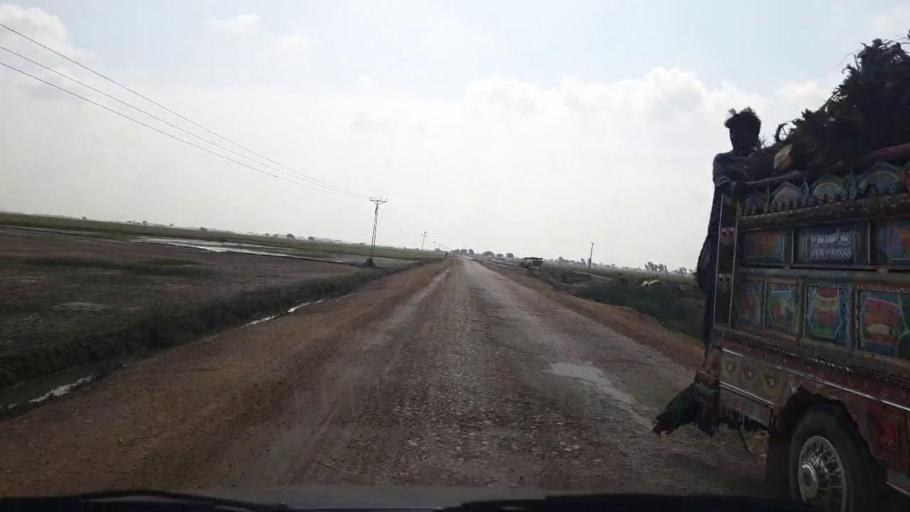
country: PK
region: Sindh
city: Kario
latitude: 24.6246
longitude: 68.5544
